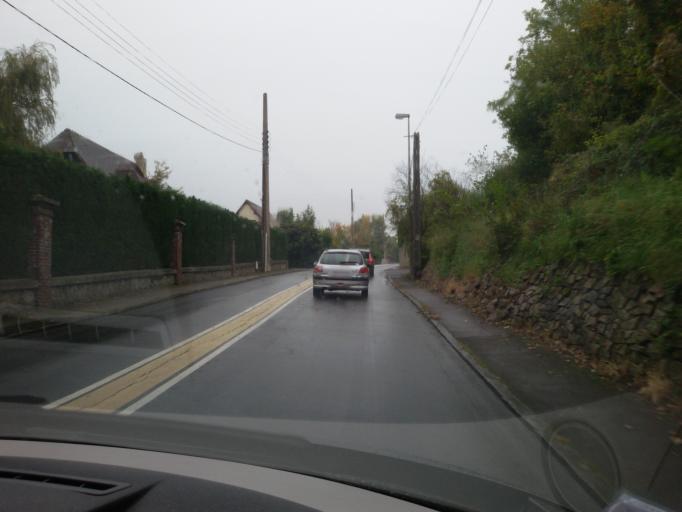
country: FR
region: Lower Normandy
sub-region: Departement du Calvados
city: Villers-sur-Mer
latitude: 49.3143
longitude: -0.0109
